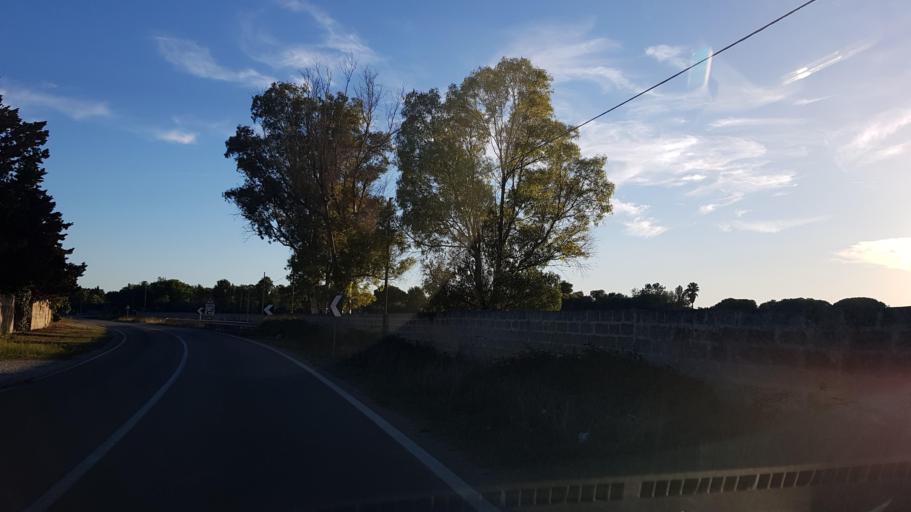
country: IT
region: Apulia
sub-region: Provincia di Lecce
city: Giorgilorio
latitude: 40.3971
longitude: 18.1946
